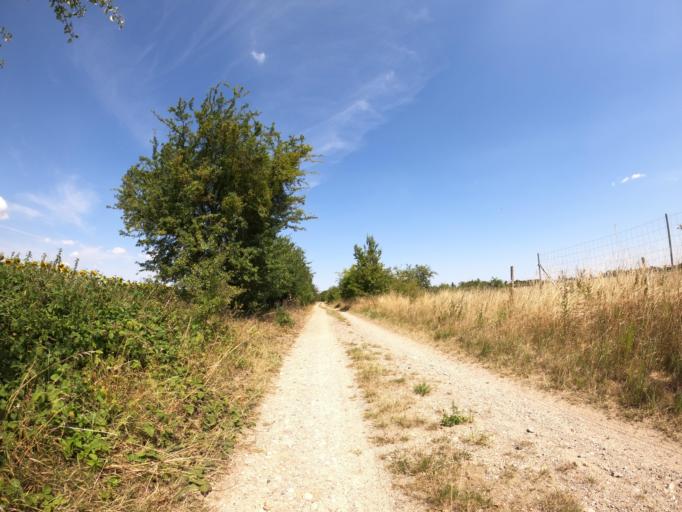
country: DE
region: Brandenburg
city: Mittenwalde
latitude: 53.2713
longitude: 13.5496
